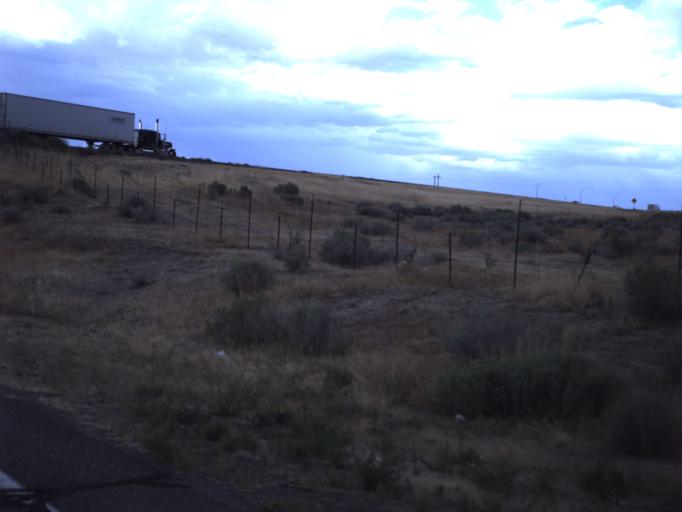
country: US
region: Utah
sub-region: Millard County
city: Fillmore
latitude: 38.9915
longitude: -112.3231
